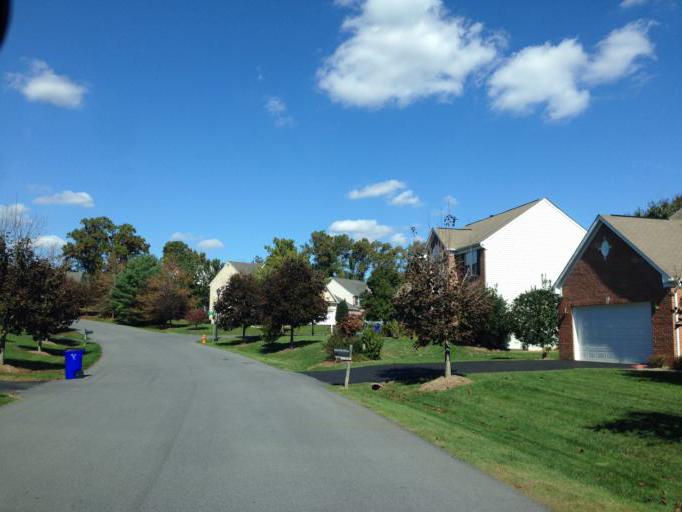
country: US
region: Maryland
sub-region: Howard County
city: North Laurel
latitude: 39.1350
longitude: -76.8987
